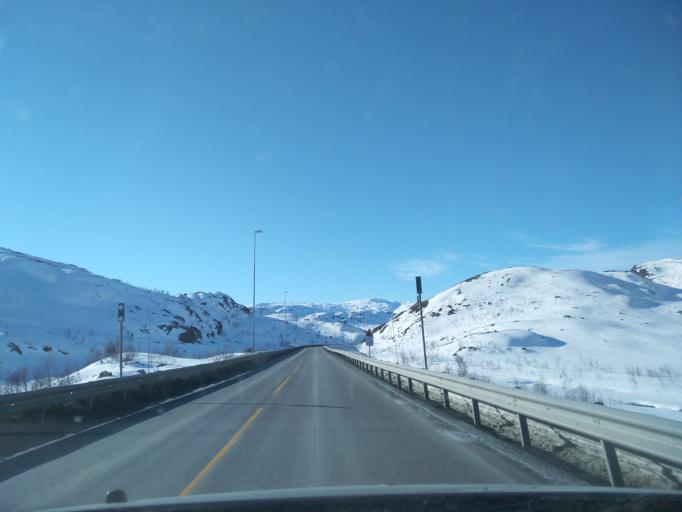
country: NO
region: Hordaland
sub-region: Odda
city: Odda
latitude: 59.8545
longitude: 6.9026
